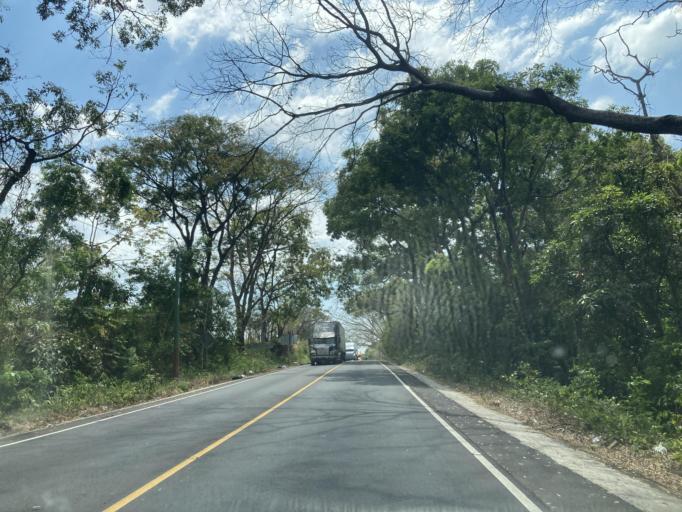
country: GT
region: Santa Rosa
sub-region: Municipio de Taxisco
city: Taxisco
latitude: 14.0742
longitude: -90.4760
